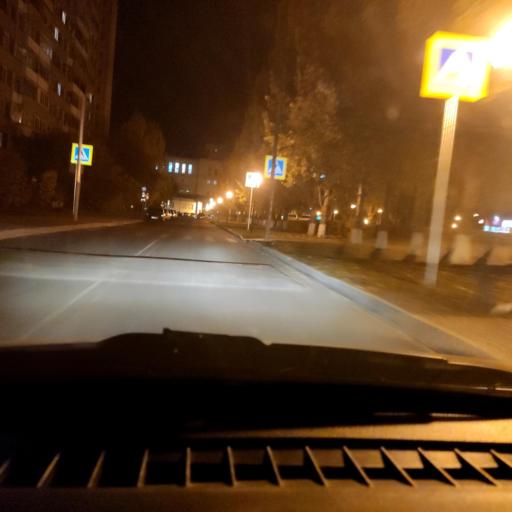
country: RU
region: Samara
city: Tol'yatti
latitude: 53.5315
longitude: 49.3188
